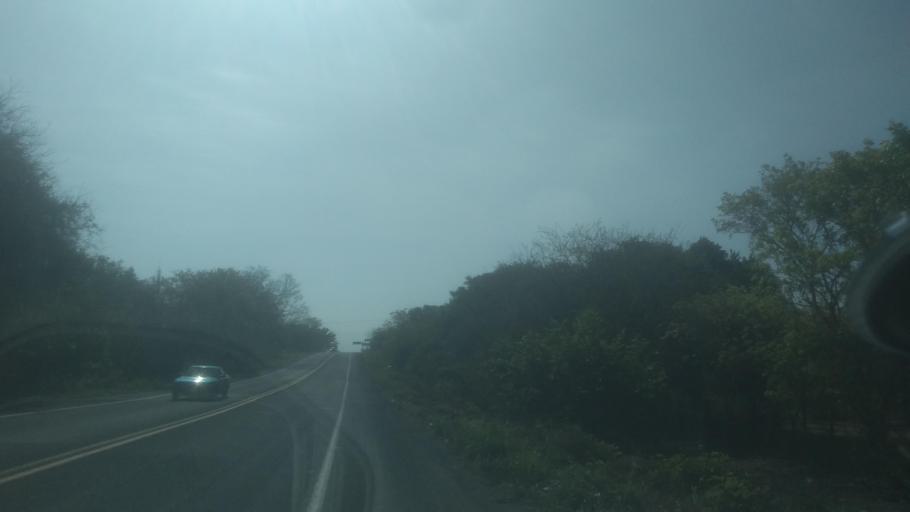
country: MX
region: Veracruz
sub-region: Emiliano Zapata
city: Plan del Rio
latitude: 19.3934
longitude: -96.6239
